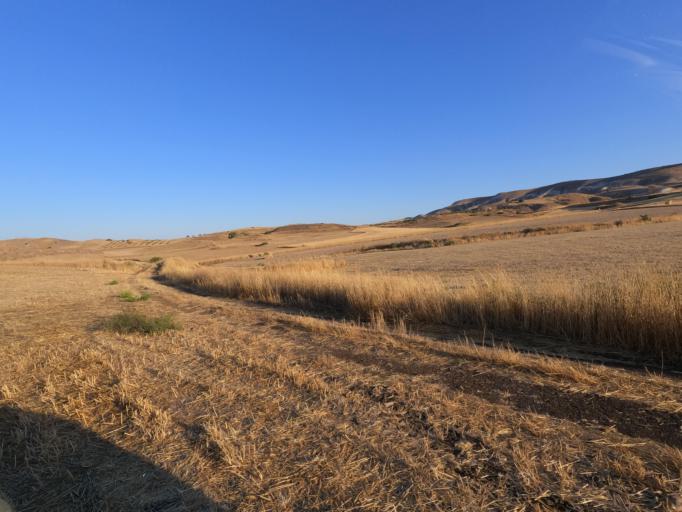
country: CY
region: Larnaka
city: Troulloi
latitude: 35.0295
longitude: 33.6395
